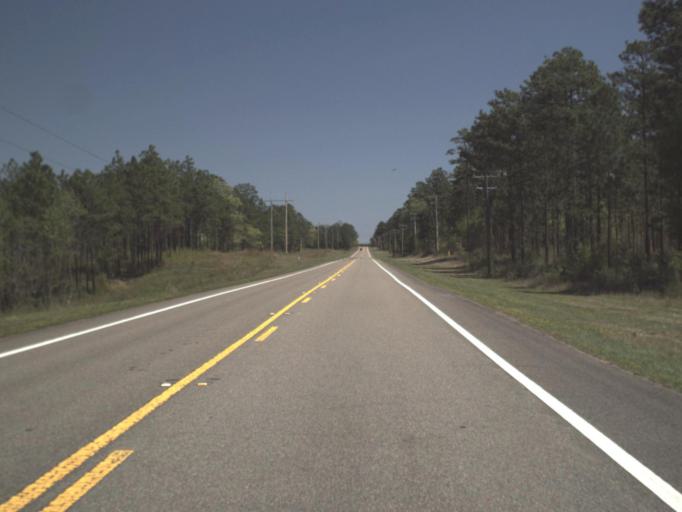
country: US
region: Florida
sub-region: Santa Rosa County
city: Point Baker
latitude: 30.8602
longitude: -86.8884
